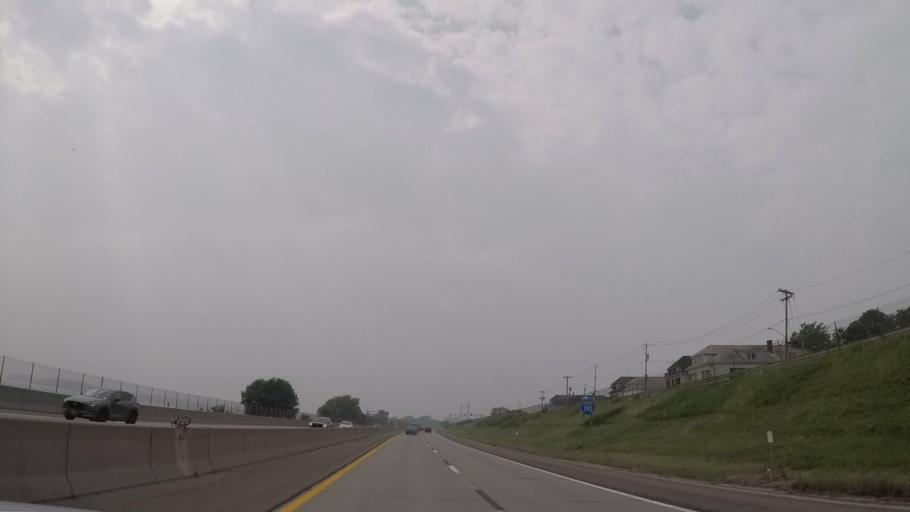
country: US
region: New York
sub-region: Erie County
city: Kenmore
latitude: 42.9577
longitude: -78.9142
